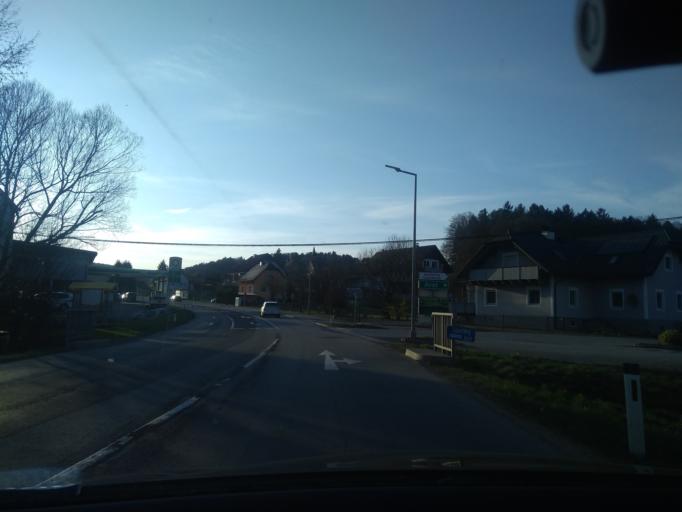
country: AT
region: Styria
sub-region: Politischer Bezirk Leibnitz
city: Empersdorf
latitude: 46.9820
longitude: 15.5669
